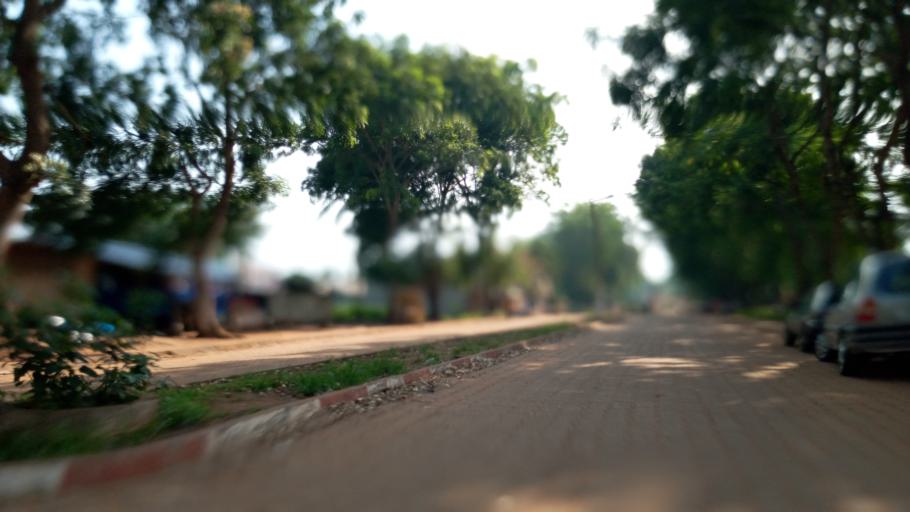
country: BJ
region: Queme
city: Porto-Novo
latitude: 6.5550
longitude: 2.6603
